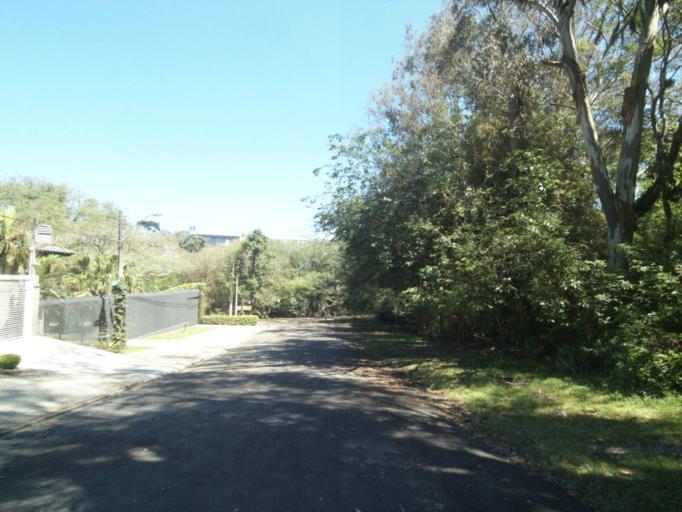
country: BR
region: Parana
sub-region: Curitiba
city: Curitiba
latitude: -25.3894
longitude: -49.2662
